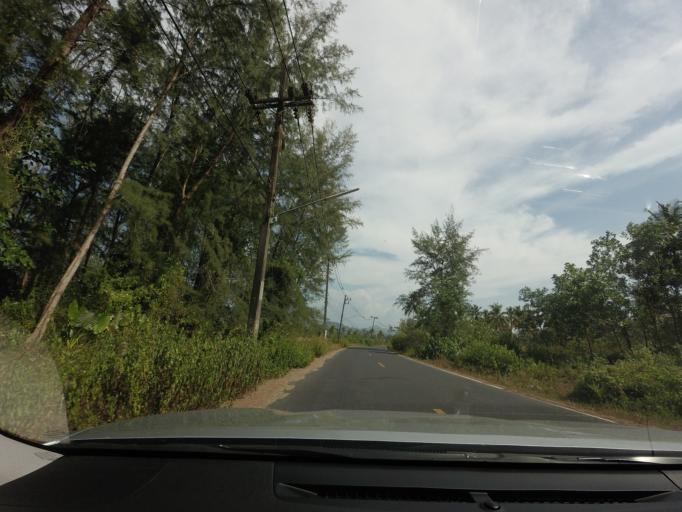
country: TH
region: Phangnga
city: Ban Khao Lak
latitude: 8.7264
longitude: 98.2403
